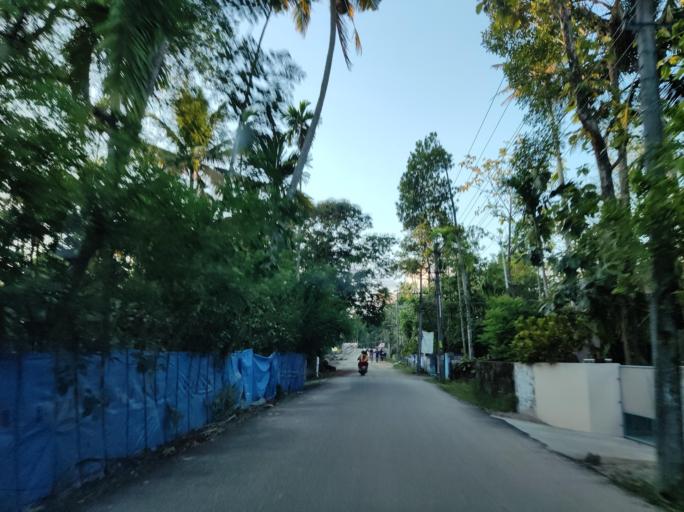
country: IN
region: Kerala
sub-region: Alappuzha
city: Vayalar
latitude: 9.7180
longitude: 76.2968
